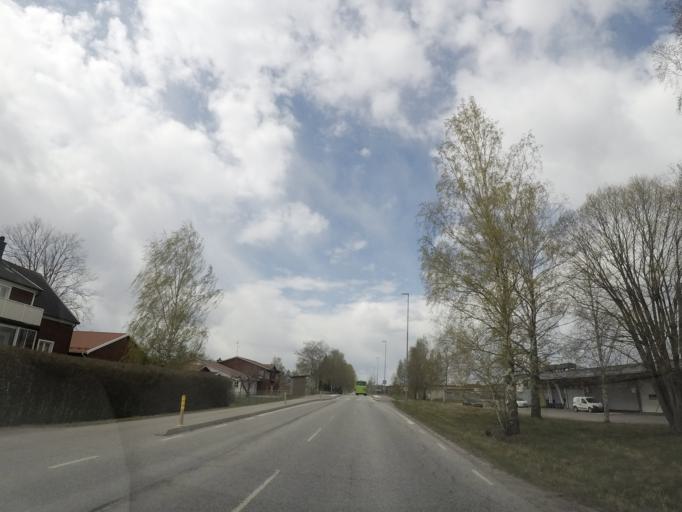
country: SE
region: Soedermanland
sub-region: Nykopings Kommun
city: Svalsta
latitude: 58.7413
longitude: 16.9197
